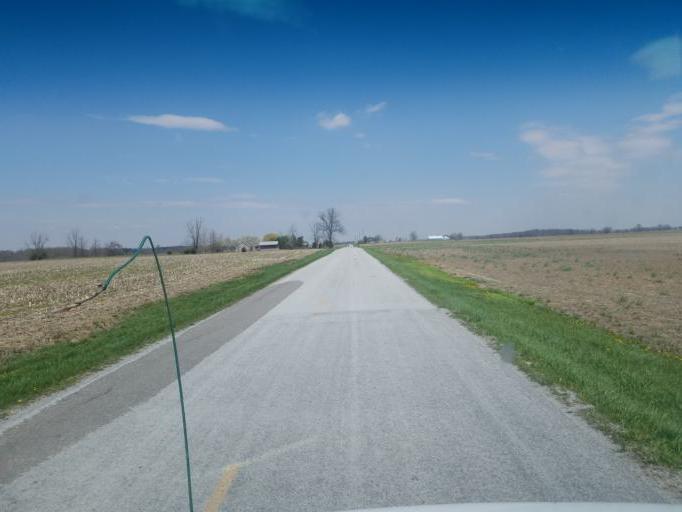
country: US
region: Ohio
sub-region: Hardin County
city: Kenton
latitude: 40.7086
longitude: -83.5379
